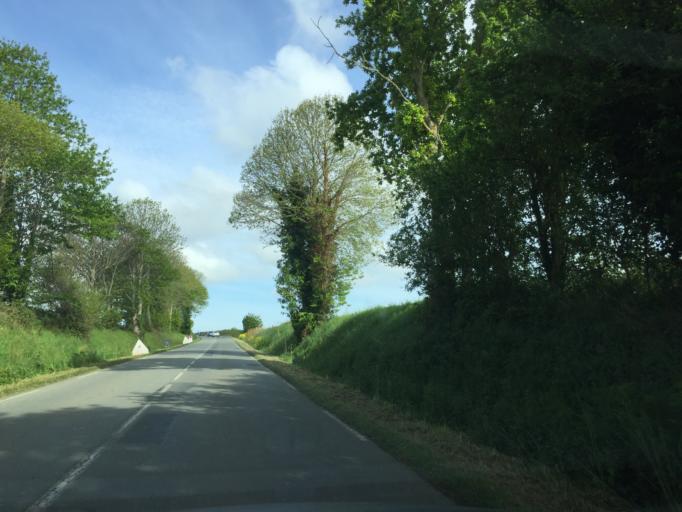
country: FR
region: Brittany
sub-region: Departement des Cotes-d'Armor
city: Matignon
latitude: 48.6047
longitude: -2.3007
